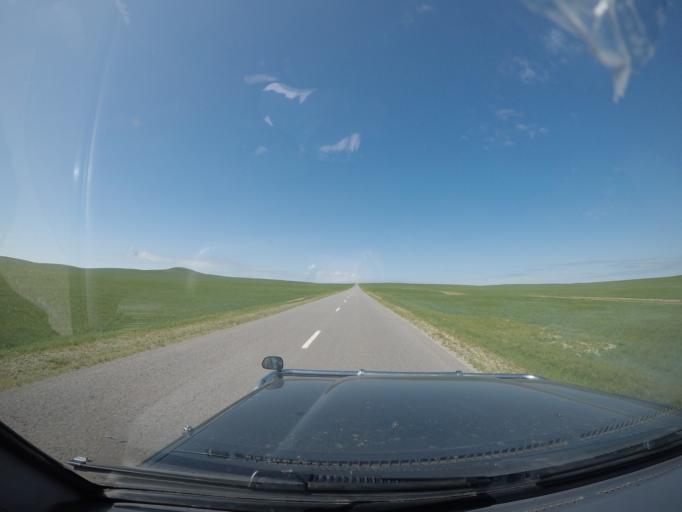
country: MN
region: Suhbaatar
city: Hanhohiy
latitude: 47.3558
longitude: 111.6905
